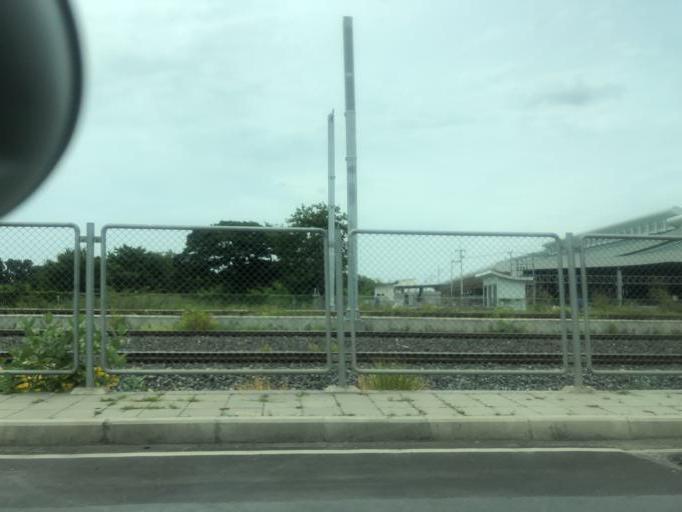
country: TH
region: Bangkok
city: Don Mueang
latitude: 13.9571
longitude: 100.6061
